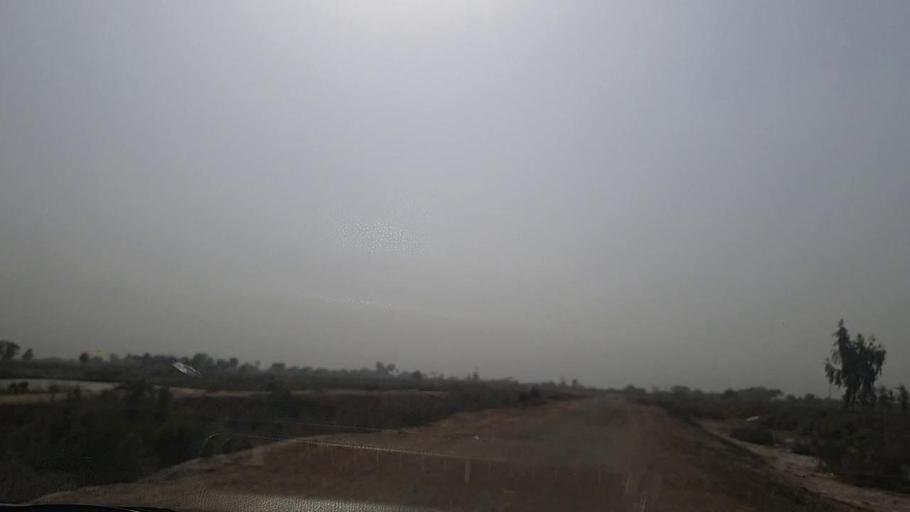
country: PK
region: Sindh
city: Pithoro
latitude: 25.4689
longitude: 69.2298
